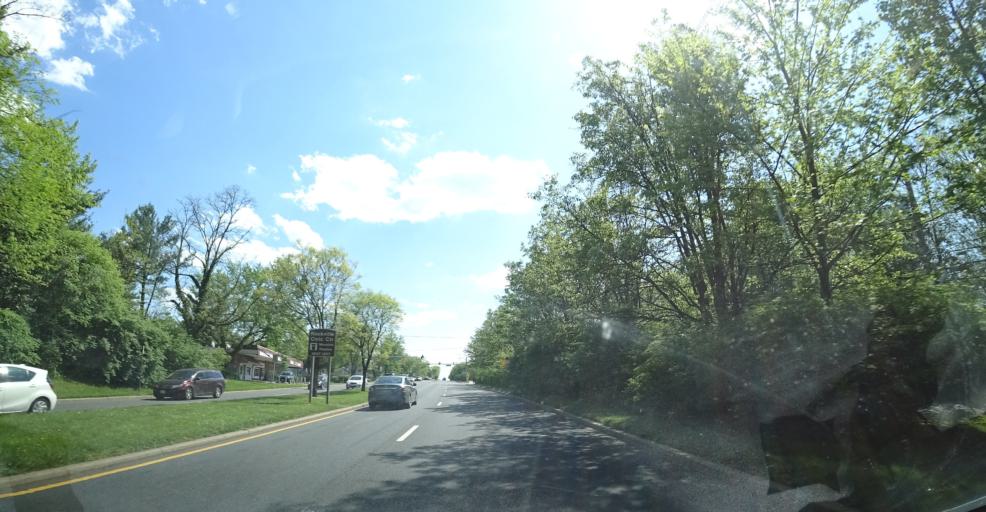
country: US
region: Maryland
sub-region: Montgomery County
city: Rockville
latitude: 39.0858
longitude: -77.1360
